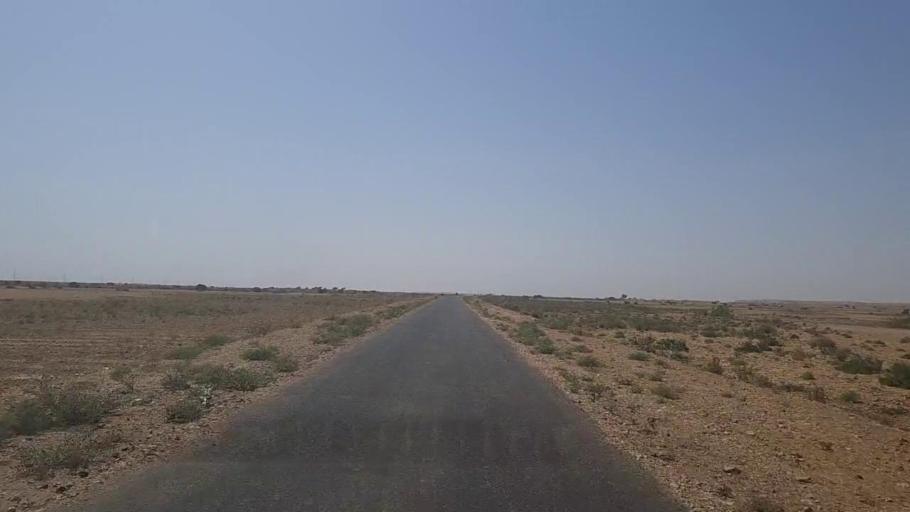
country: PK
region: Sindh
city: Kotri
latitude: 25.1523
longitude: 68.2299
